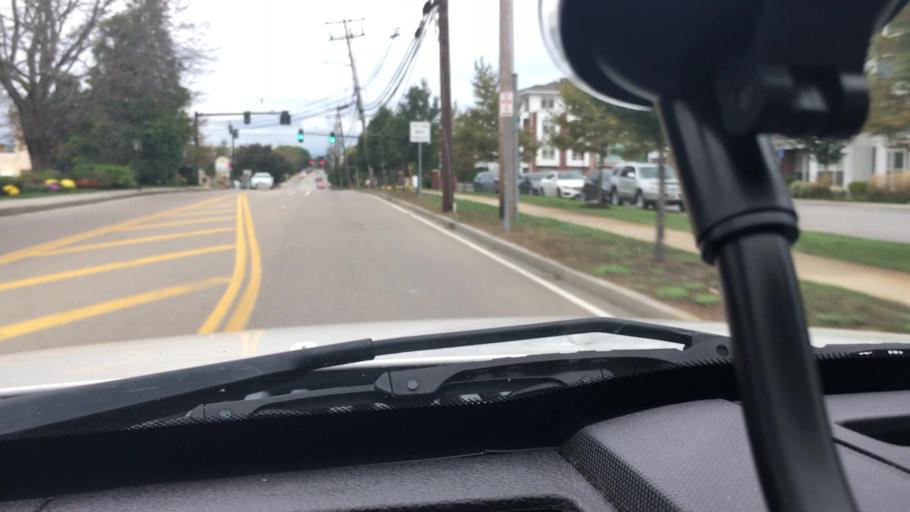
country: US
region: Massachusetts
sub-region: Middlesex County
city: Waltham
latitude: 42.3665
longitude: -71.2102
